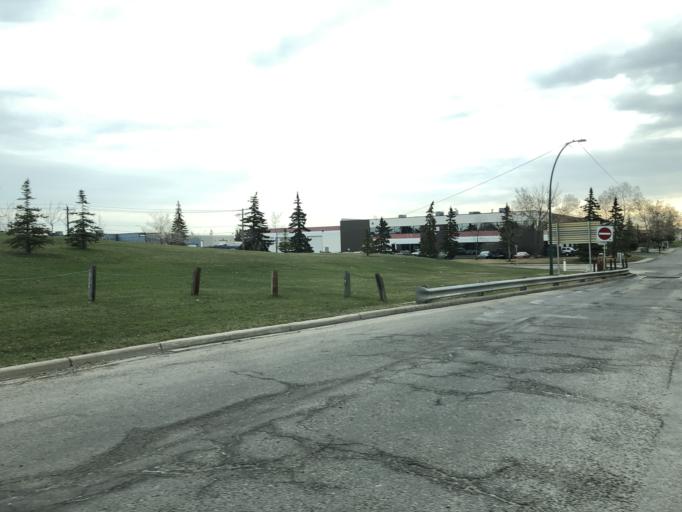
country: CA
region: Alberta
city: Calgary
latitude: 51.0741
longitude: -114.0102
